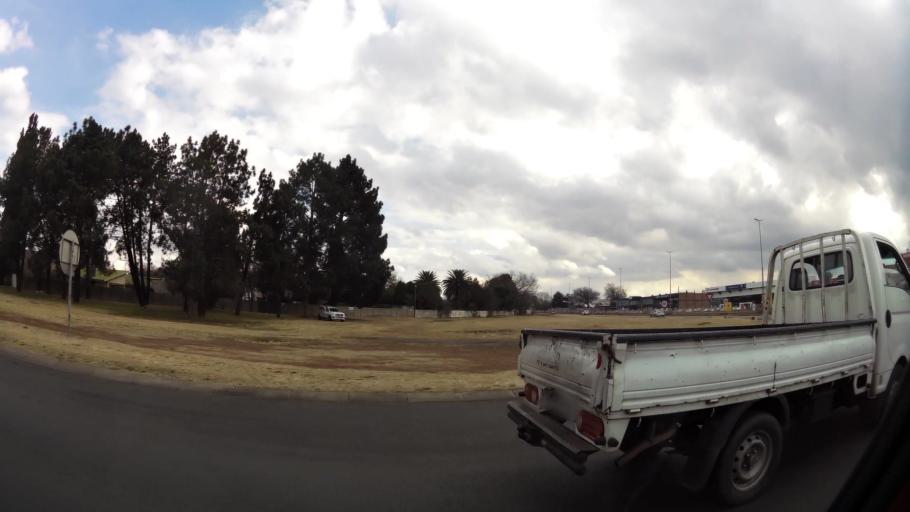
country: ZA
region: Gauteng
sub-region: Sedibeng District Municipality
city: Vanderbijlpark
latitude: -26.7067
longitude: 27.8359
